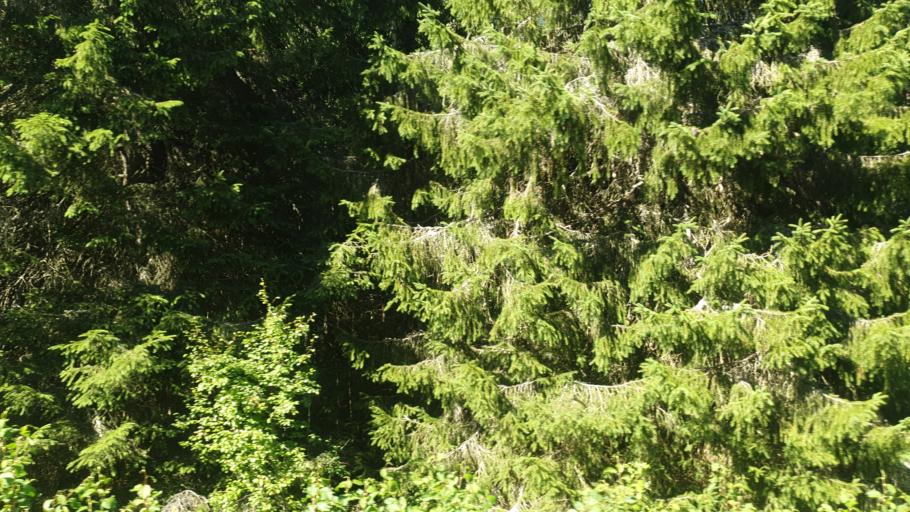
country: NO
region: Sor-Trondelag
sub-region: Meldal
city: Meldal
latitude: 63.1427
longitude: 9.7128
